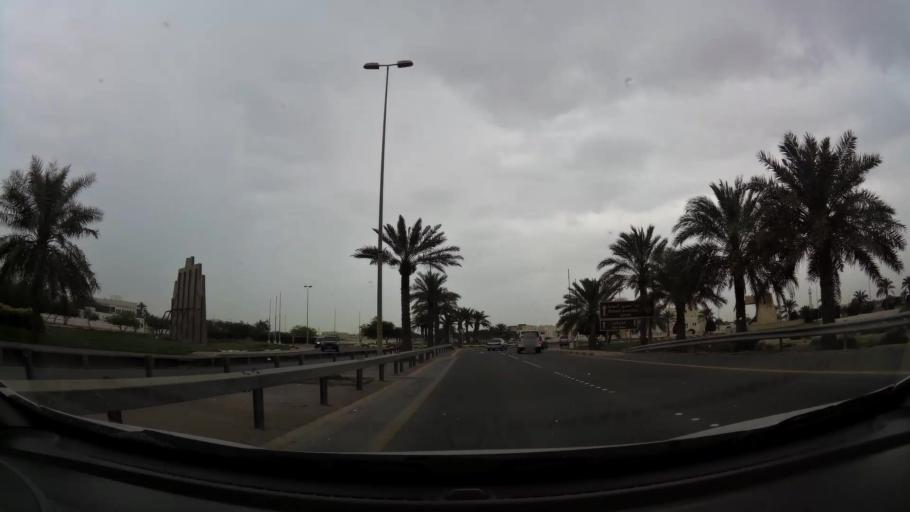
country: BH
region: Northern
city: Ar Rifa'
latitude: 26.1088
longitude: 50.5391
